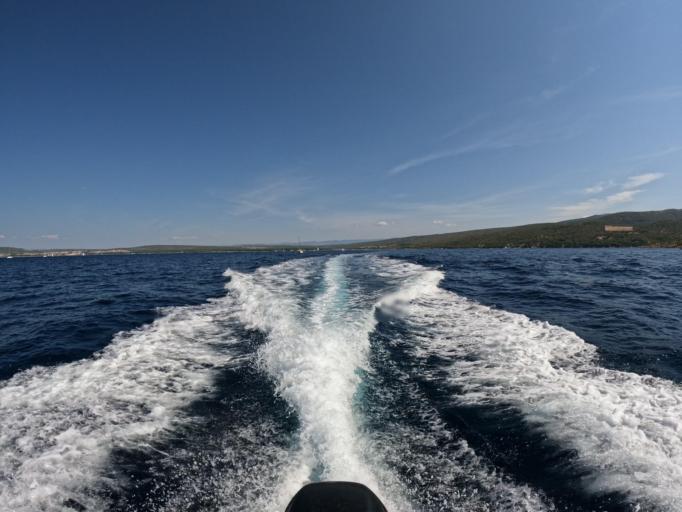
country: HR
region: Primorsko-Goranska
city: Punat
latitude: 44.9856
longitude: 14.6121
